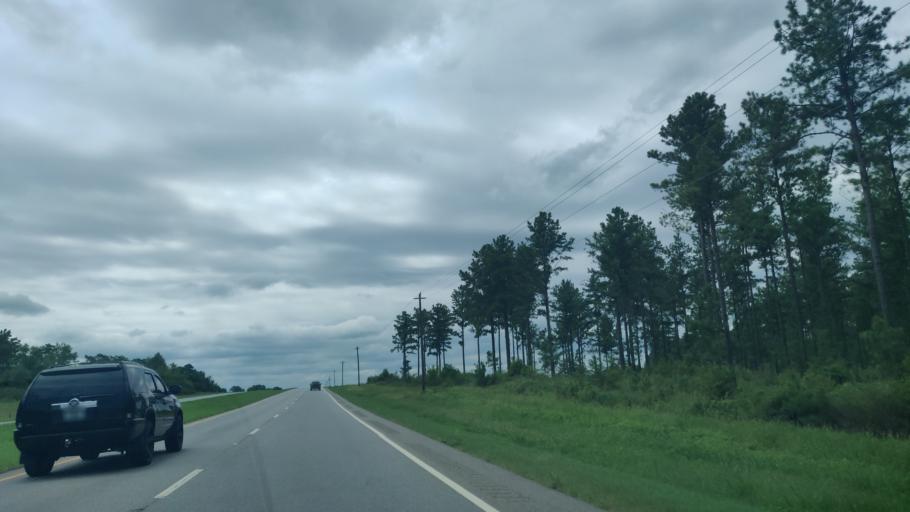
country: US
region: Georgia
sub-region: Terrell County
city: Dawson
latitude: 31.8297
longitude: -84.4640
